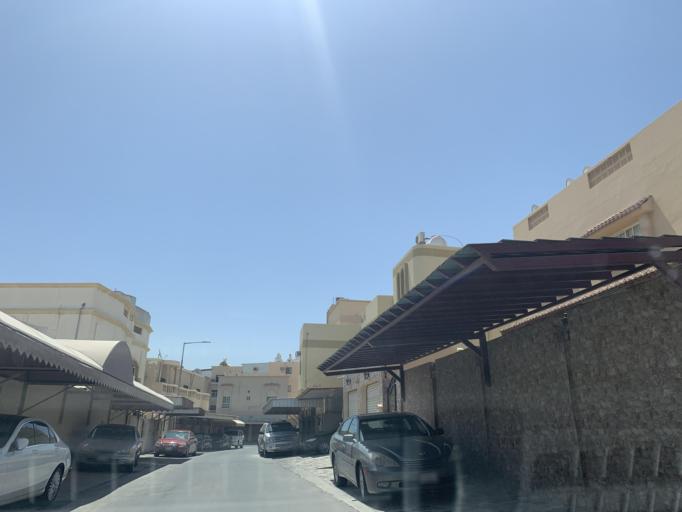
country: BH
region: Northern
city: Ar Rifa'
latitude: 26.1364
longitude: 50.5763
